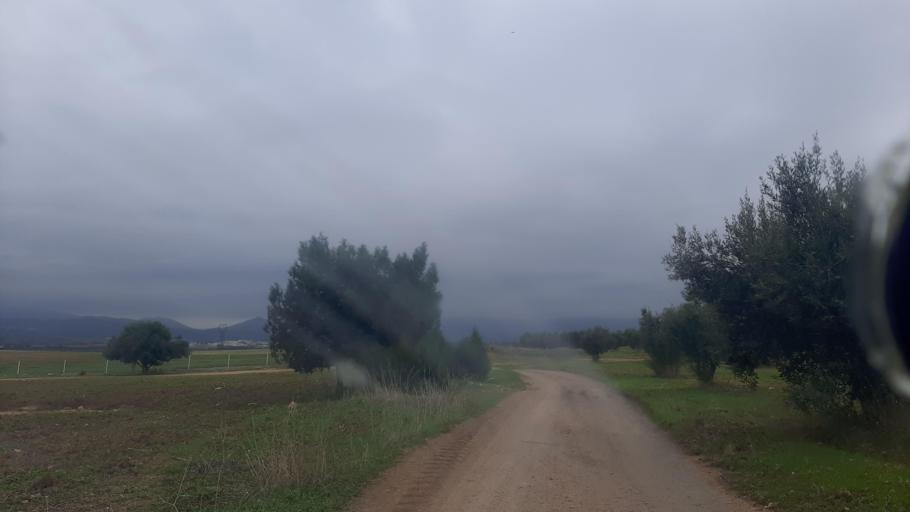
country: TN
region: Tunis
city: La Sebala du Mornag
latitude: 36.5698
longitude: 10.2943
